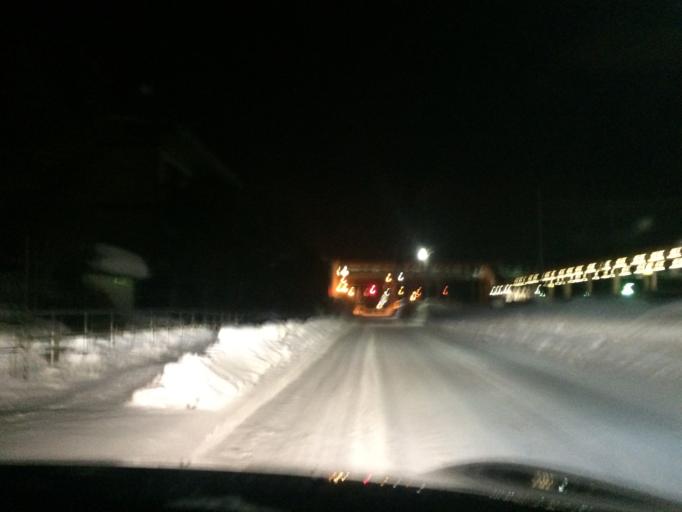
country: JP
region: Hokkaido
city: Sapporo
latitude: 43.0474
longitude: 141.4371
